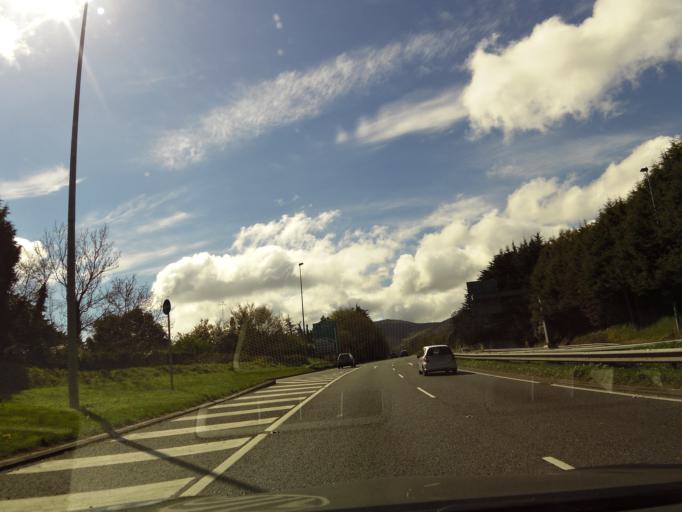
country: IE
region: Leinster
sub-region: Wicklow
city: Kilmacanoge
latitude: 53.1812
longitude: -6.1351
